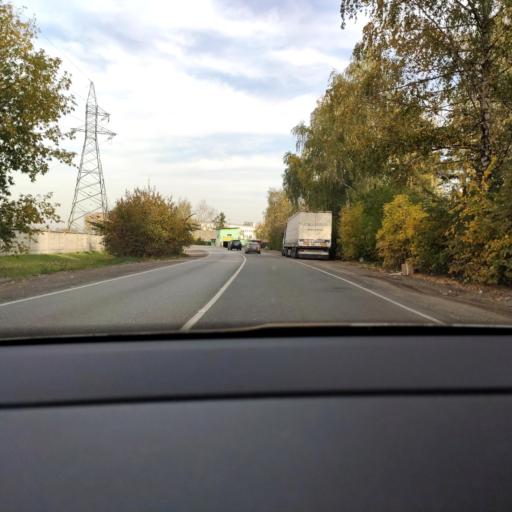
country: RU
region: Moskovskaya
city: Lesnyye Polyany
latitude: 55.9753
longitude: 37.8668
